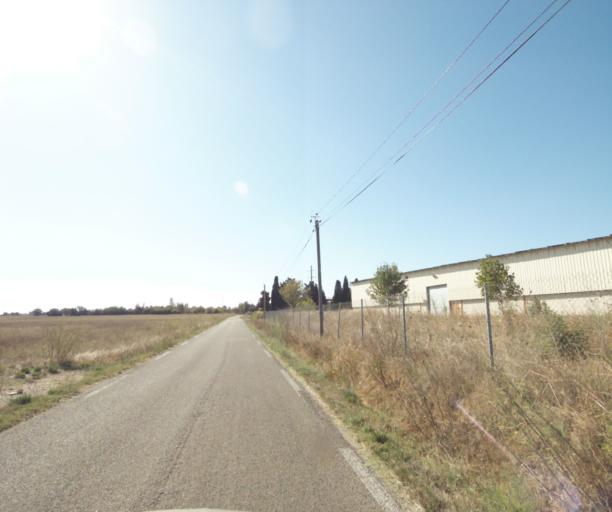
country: FR
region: Languedoc-Roussillon
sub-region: Departement du Gard
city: Rodilhan
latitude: 43.8179
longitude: 4.4284
